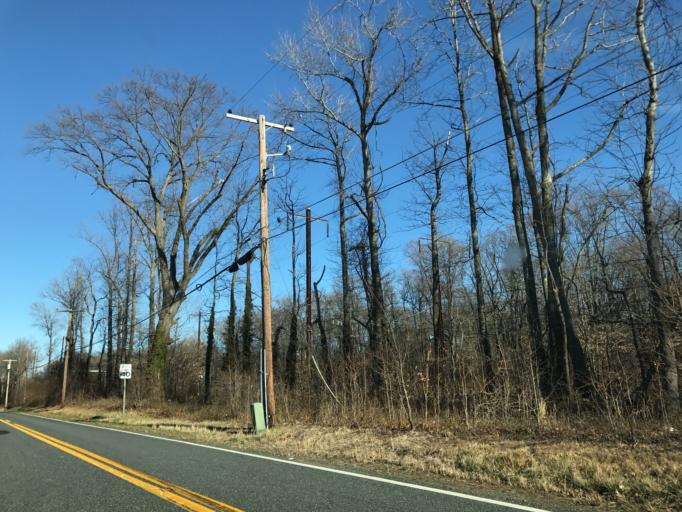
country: US
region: Maryland
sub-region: Harford County
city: Riverside
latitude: 39.4411
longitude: -76.2349
